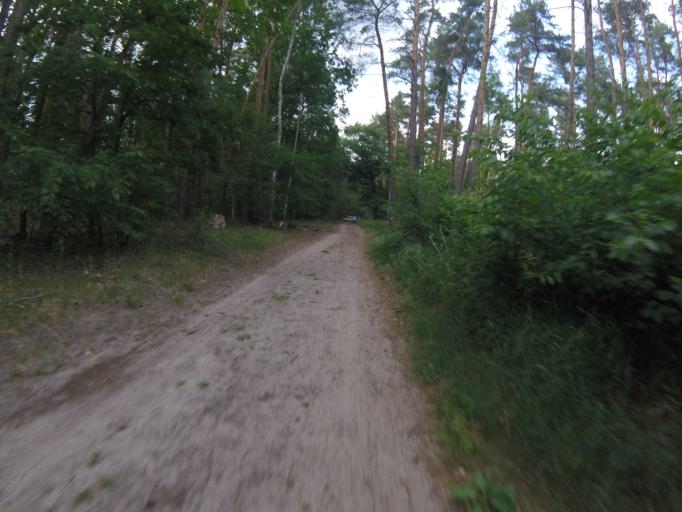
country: DE
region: Brandenburg
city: Konigs Wusterhausen
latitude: 52.2694
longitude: 13.6096
